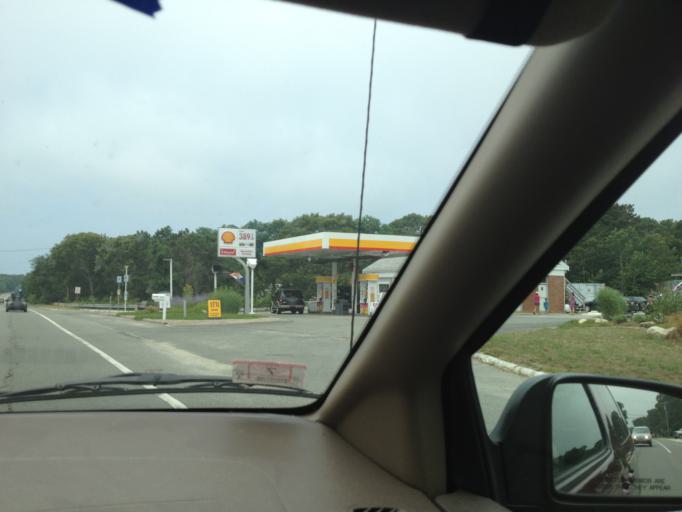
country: US
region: Massachusetts
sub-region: Barnstable County
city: Wellfleet
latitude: 41.9172
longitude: -69.9942
